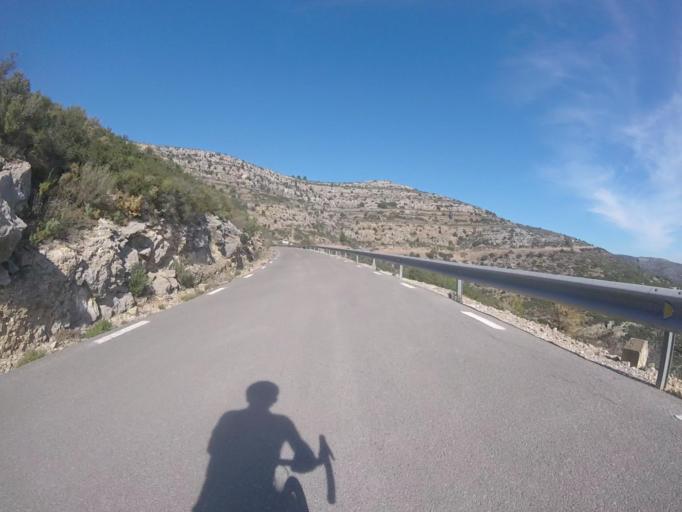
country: ES
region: Valencia
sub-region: Provincia de Castello
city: Sarratella
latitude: 40.2818
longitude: 0.0380
